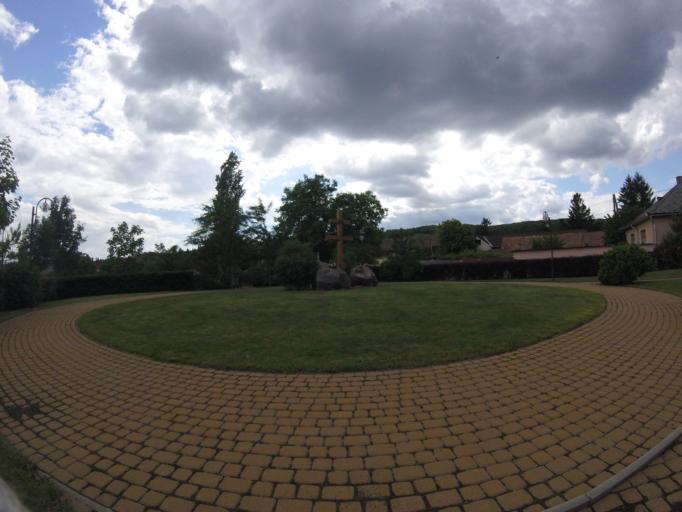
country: HU
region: Heves
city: Abasar
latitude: 47.8276
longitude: 20.0548
